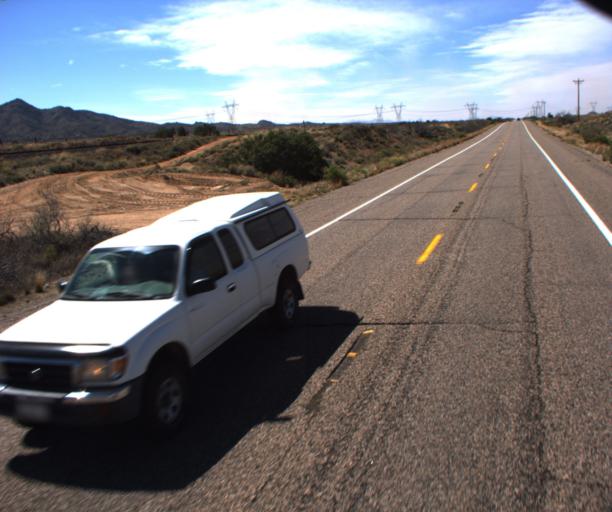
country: US
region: Arizona
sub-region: Mohave County
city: New Kingman-Butler
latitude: 35.3890
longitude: -113.7395
